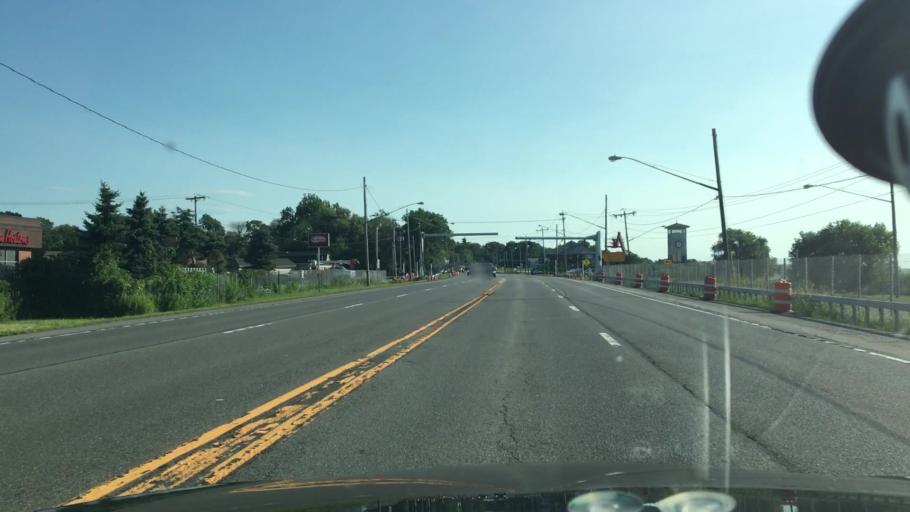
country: US
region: New York
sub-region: Erie County
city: Blasdell
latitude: 42.7748
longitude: -78.8625
